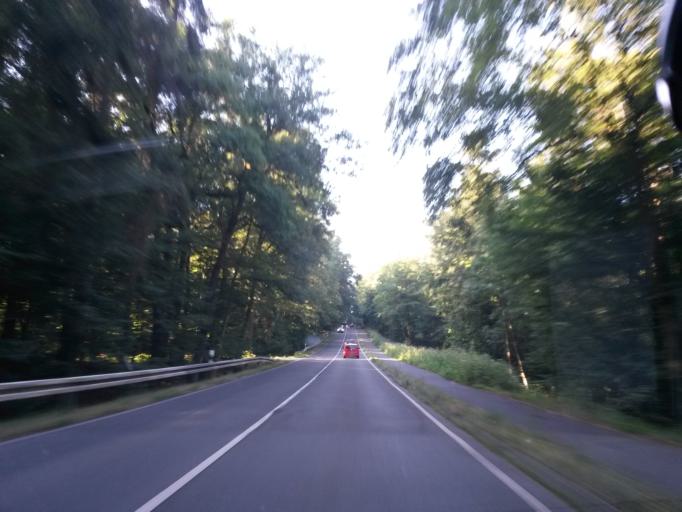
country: DE
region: North Rhine-Westphalia
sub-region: Regierungsbezirk Koln
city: Rosrath
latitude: 50.9432
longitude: 7.1682
